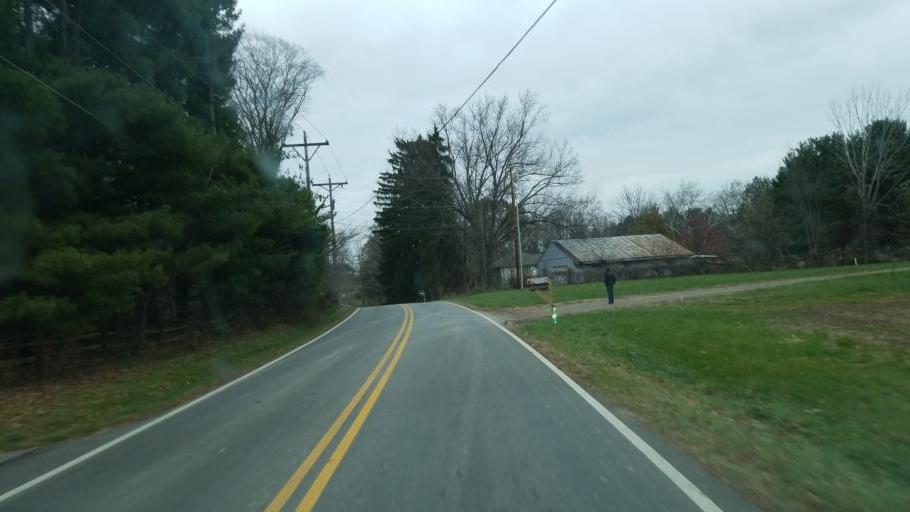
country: US
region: Ohio
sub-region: Franklin County
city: New Albany
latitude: 40.1499
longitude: -82.8400
